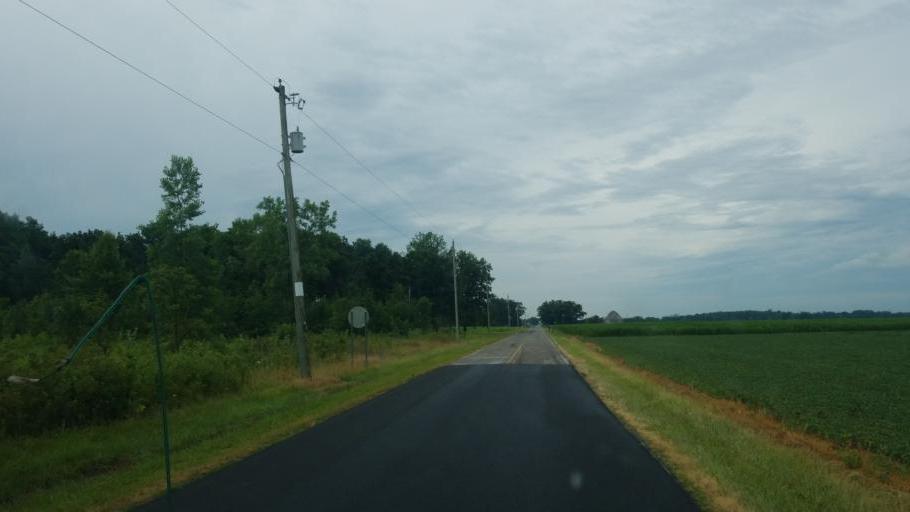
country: US
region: Ohio
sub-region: Defiance County
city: Hicksville
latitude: 41.2898
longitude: -84.6895
